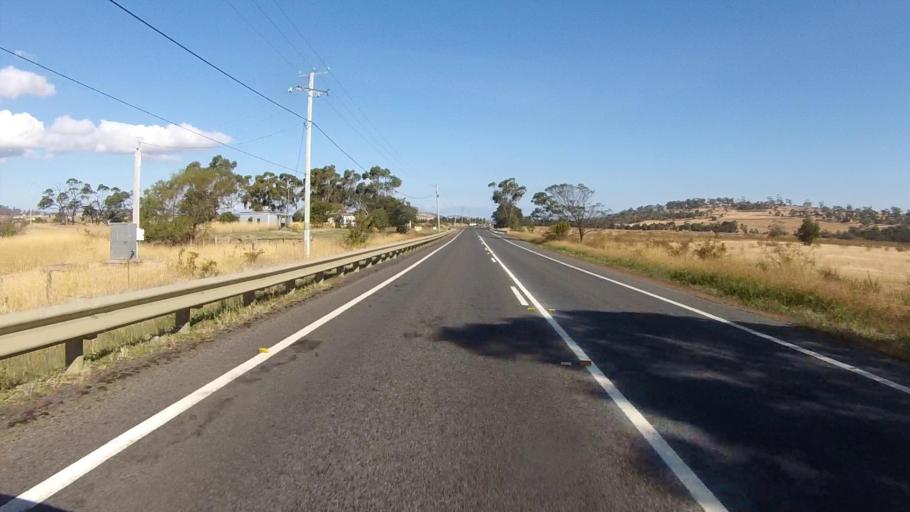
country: AU
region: Tasmania
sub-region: Sorell
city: Sorell
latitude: -42.7179
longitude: 147.5179
